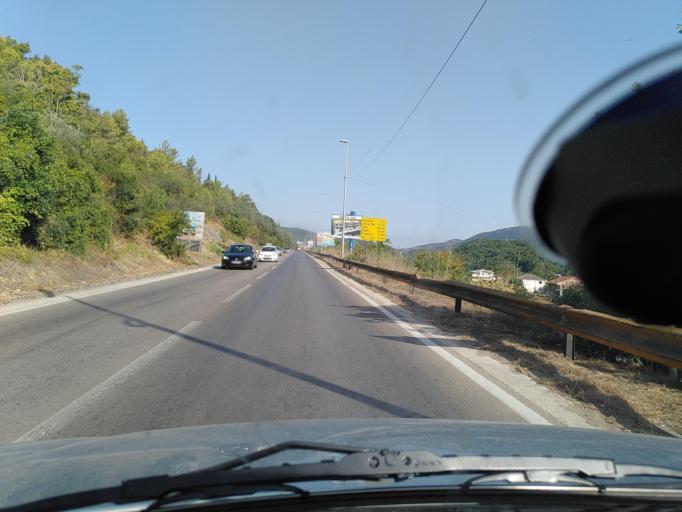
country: ME
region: Ulcinj
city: Ulcinj
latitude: 41.9388
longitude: 19.2165
